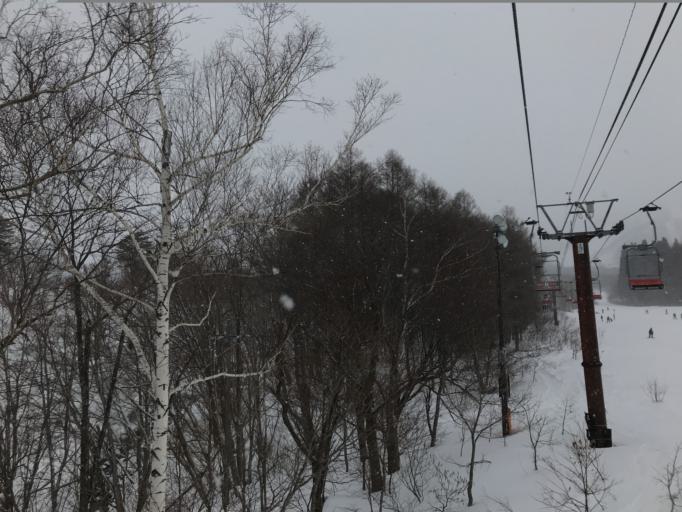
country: JP
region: Nagano
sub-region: Kitaazumi Gun
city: Hakuba
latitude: 36.7520
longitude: 137.8668
